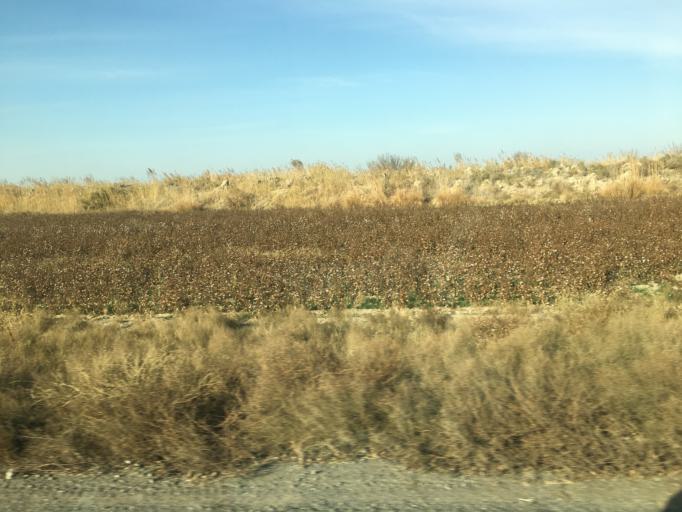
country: TM
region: Mary
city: Mary
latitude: 37.6015
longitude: 61.6601
